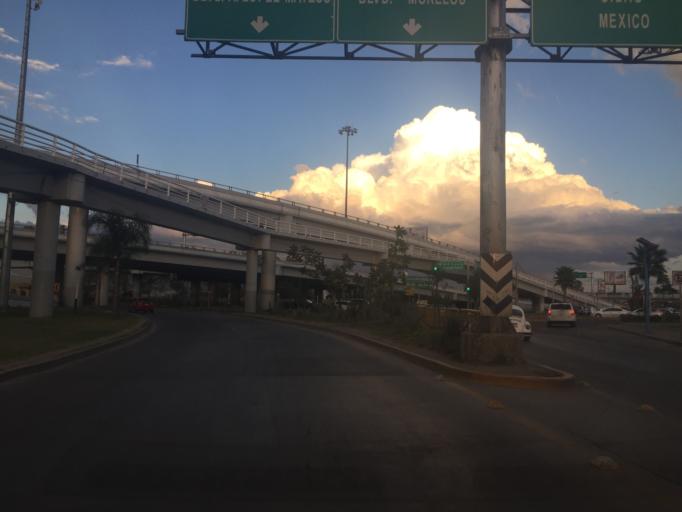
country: MX
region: Guanajuato
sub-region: Leon
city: Fraccionamiento Paraiso Real
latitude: 21.0947
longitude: -101.6275
